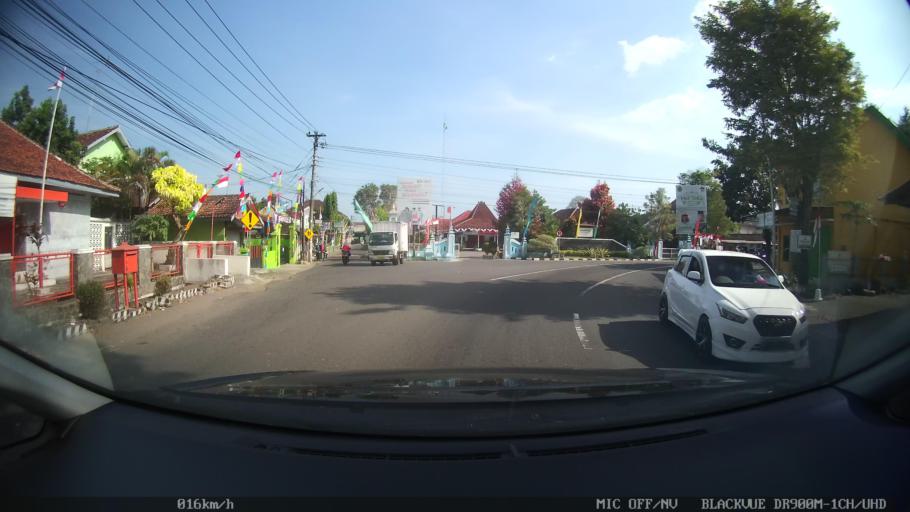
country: ID
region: Daerah Istimewa Yogyakarta
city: Kasihan
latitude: -7.8276
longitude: 110.3450
